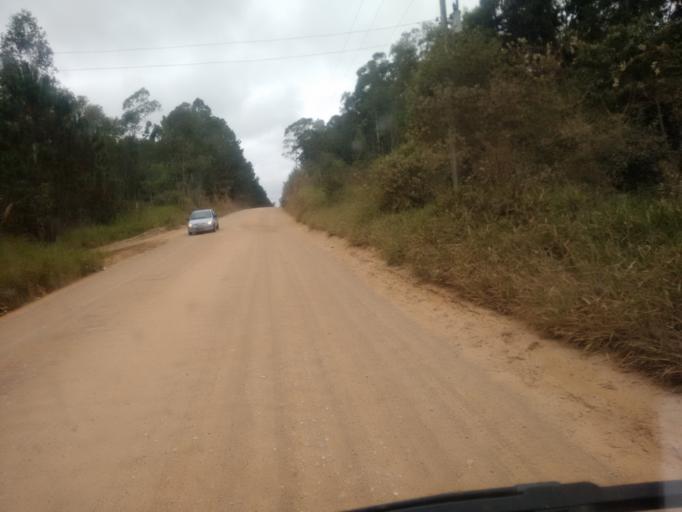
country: BR
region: Rio Grande do Sul
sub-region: Camaqua
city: Camaqua
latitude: -30.8036
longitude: -51.8295
